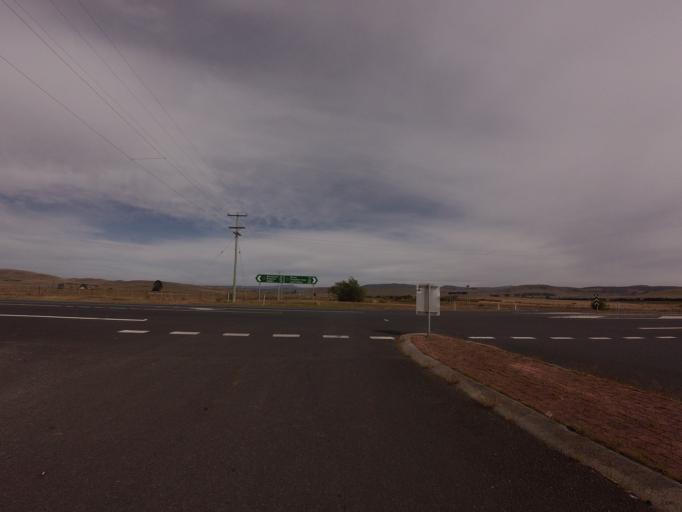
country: AU
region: Tasmania
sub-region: Brighton
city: Bridgewater
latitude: -42.3092
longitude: 147.3572
